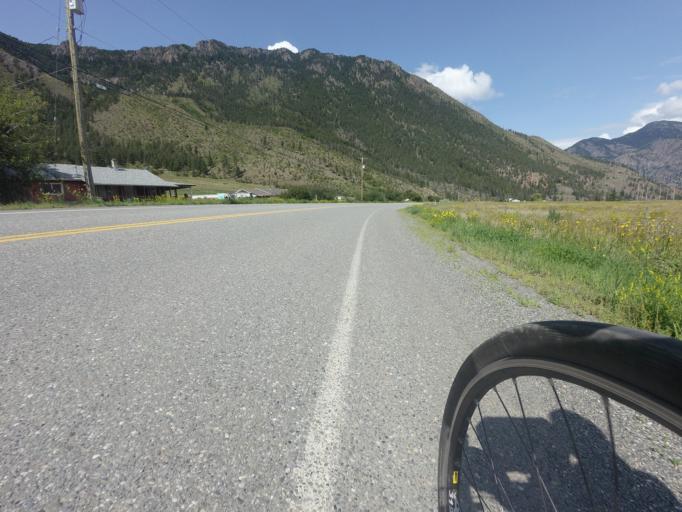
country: CA
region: British Columbia
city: Lillooet
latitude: 50.7420
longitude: -121.8833
